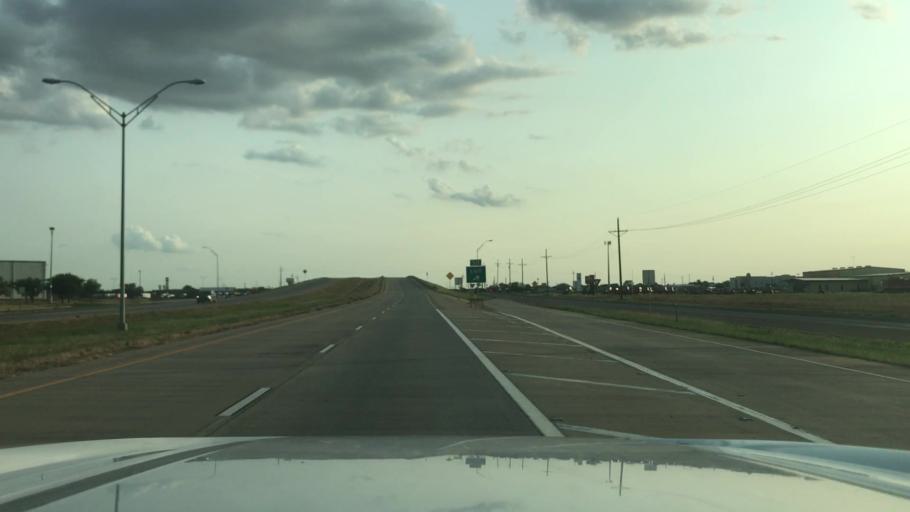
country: US
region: Texas
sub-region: Hale County
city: Plainview
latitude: 34.2139
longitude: -101.7318
